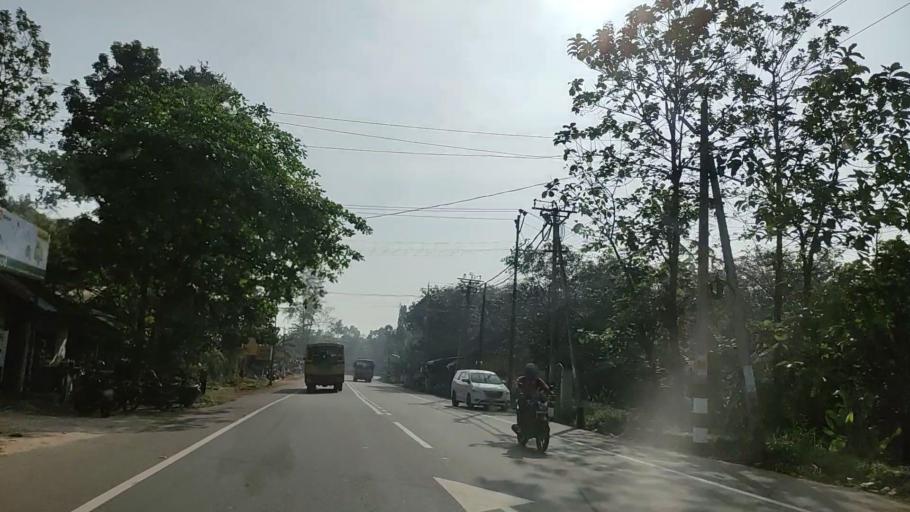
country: IN
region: Kerala
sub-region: Kollam
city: Punalur
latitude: 8.9842
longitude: 76.8059
